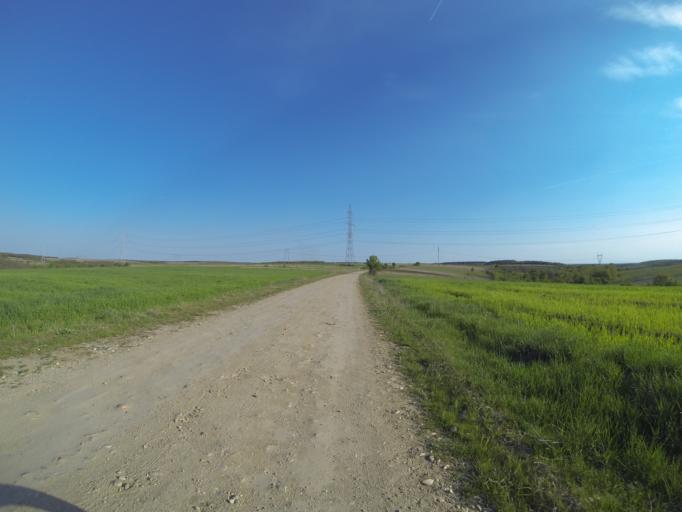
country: RO
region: Dolj
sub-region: Comuna Filiasi
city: Fratostita
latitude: 44.5717
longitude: 23.5877
